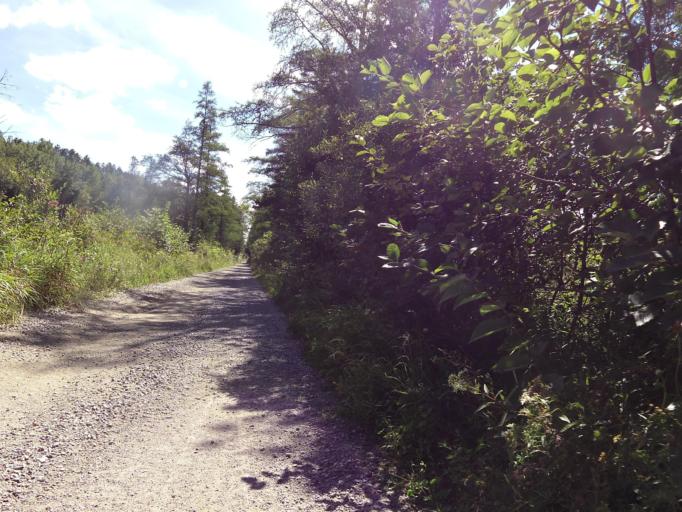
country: CA
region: Ontario
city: Renfrew
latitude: 45.0413
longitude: -76.7022
